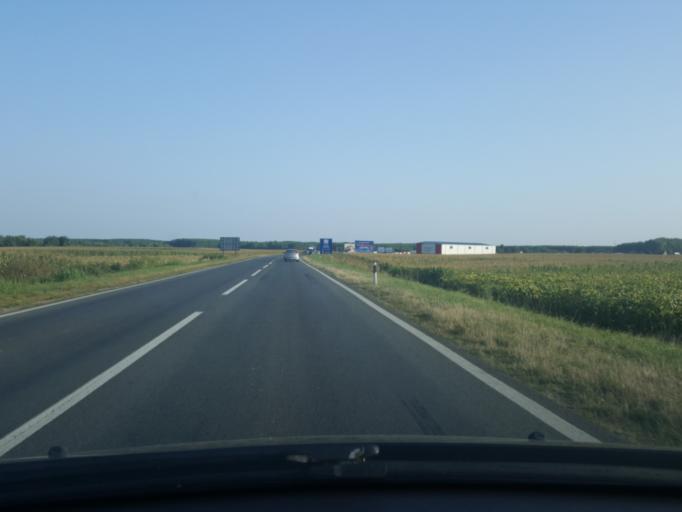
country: RS
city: Klenak
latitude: 44.7715
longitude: 19.7259
